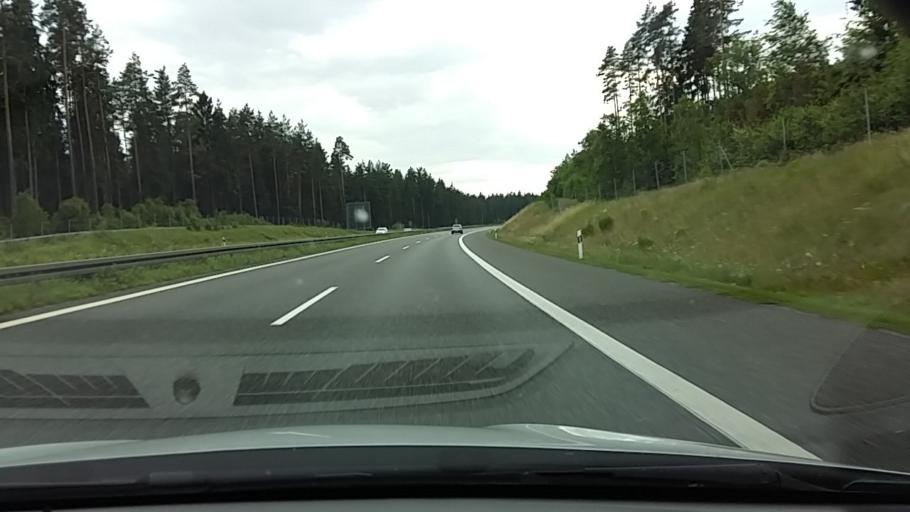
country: DE
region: Bavaria
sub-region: Upper Palatinate
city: Moosbach
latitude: 49.6152
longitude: 12.4109
